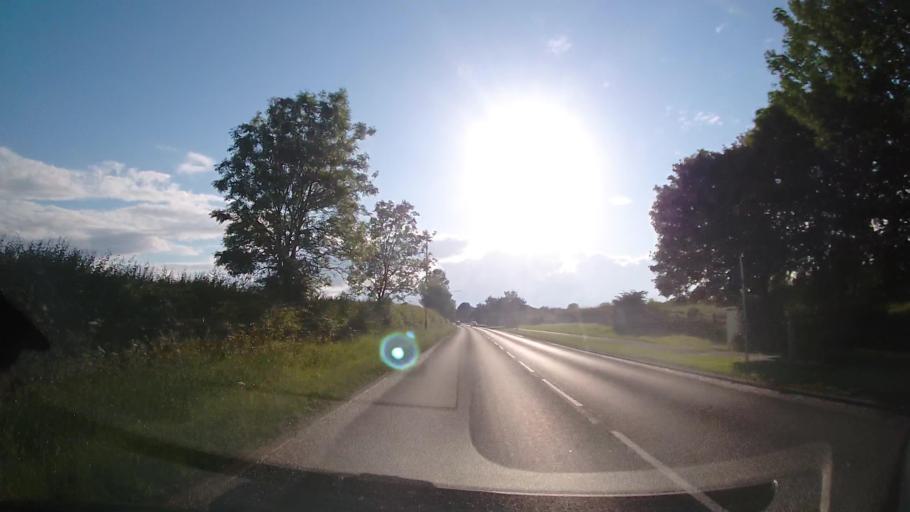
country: GB
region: England
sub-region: Leicestershire
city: Kirby Muxloe
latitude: 52.6530
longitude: -1.2297
